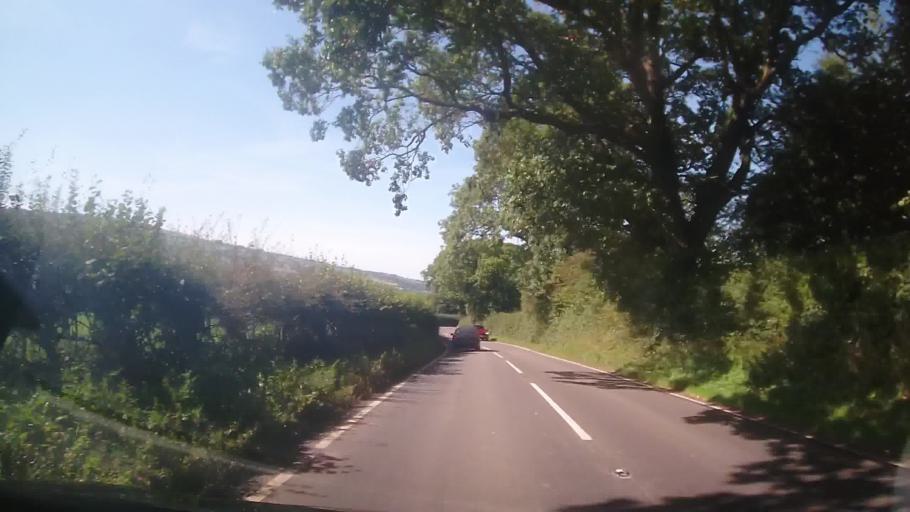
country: GB
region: England
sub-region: Shropshire
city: Lydham
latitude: 52.5214
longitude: -3.0003
